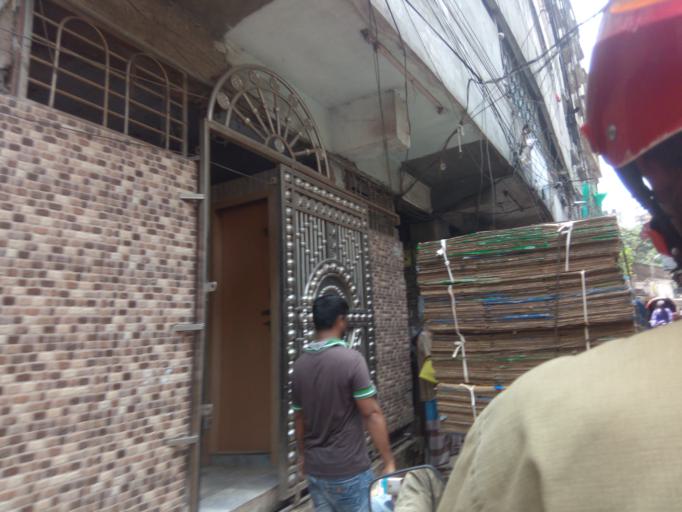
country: BD
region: Dhaka
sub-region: Dhaka
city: Dhaka
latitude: 23.7145
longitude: 90.4042
